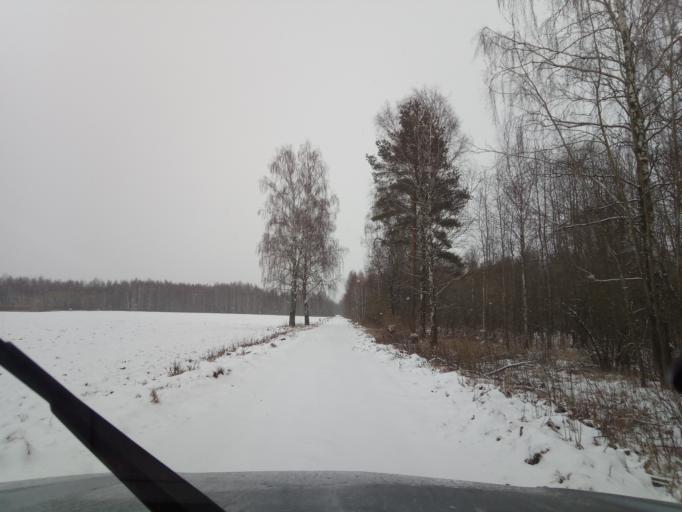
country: LT
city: Ramygala
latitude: 55.5868
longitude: 24.3722
